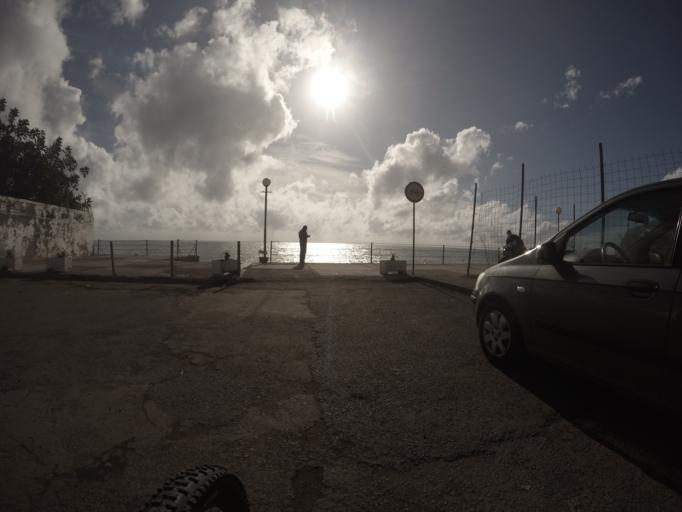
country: PT
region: Madeira
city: Camara de Lobos
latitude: 32.6411
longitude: -16.9522
